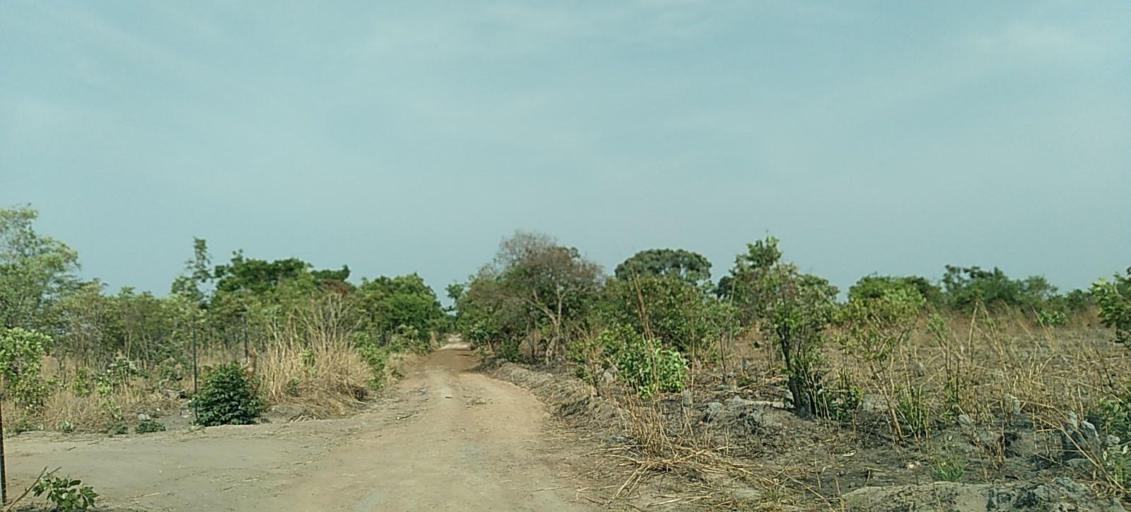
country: ZM
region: Copperbelt
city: Luanshya
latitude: -13.2172
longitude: 28.6492
